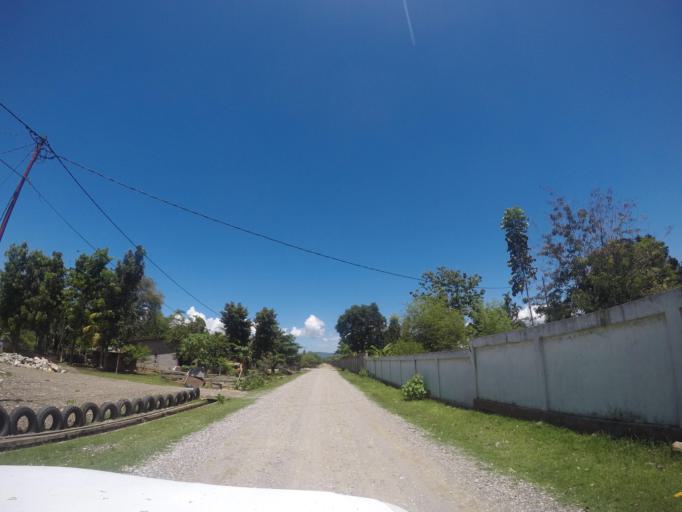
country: TL
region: Bobonaro
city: Maliana
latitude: -8.9784
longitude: 125.2193
